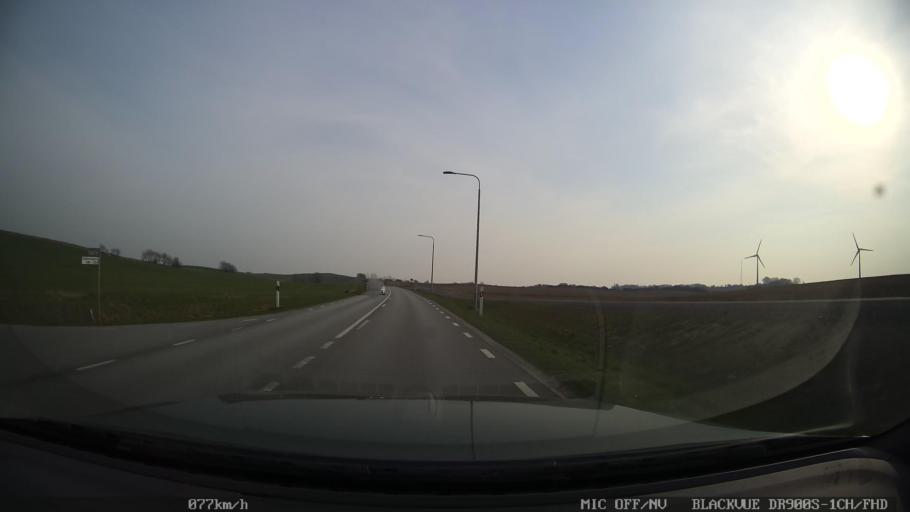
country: SE
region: Skane
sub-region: Ystads Kommun
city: Ystad
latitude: 55.4687
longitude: 13.7971
